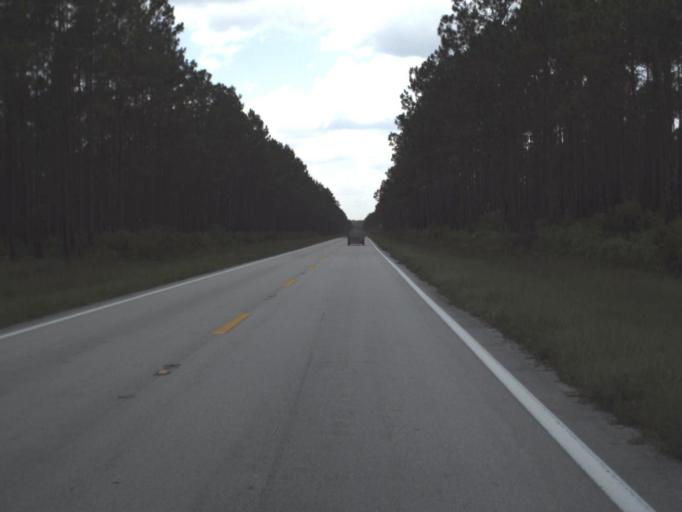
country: US
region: Florida
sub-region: Baker County
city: Macclenny
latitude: 30.5589
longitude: -82.3804
